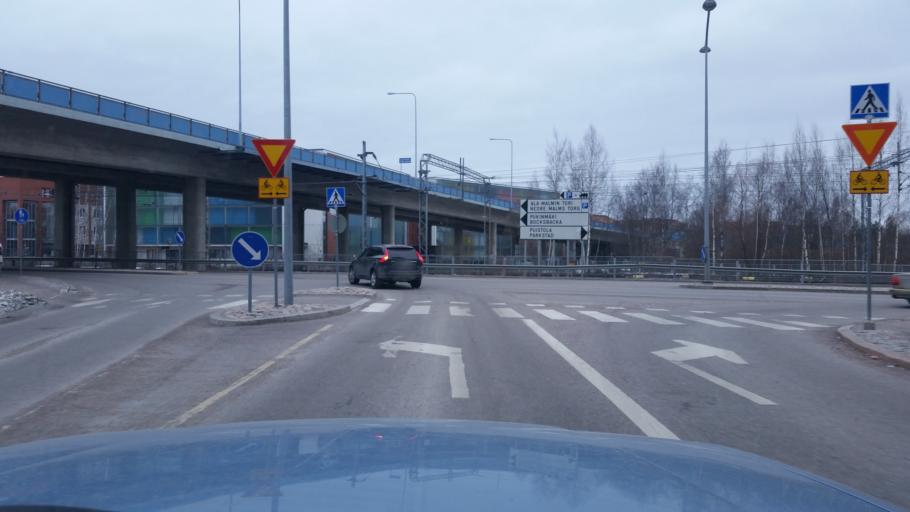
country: FI
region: Uusimaa
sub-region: Helsinki
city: Vantaa
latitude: 60.2543
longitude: 25.0175
